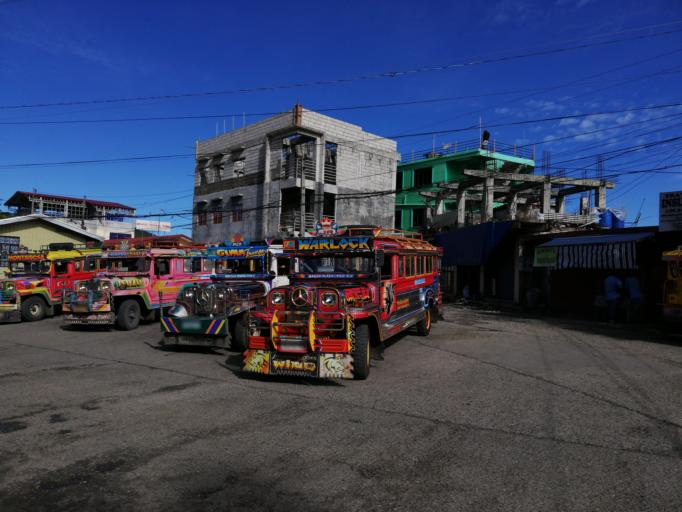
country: PH
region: Cordillera
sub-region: Province of Benguet
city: La Trinidad
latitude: 16.4555
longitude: 120.5695
